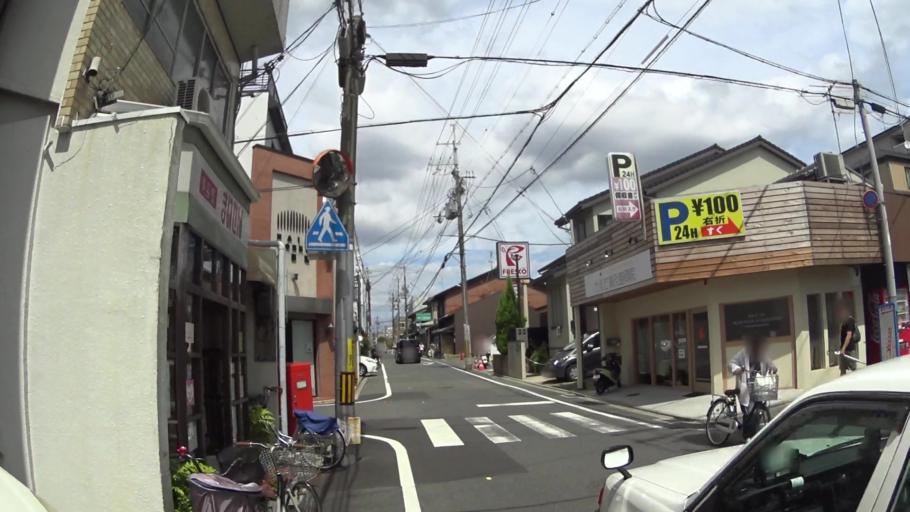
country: JP
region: Kyoto
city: Kyoto
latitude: 34.9644
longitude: 135.7711
